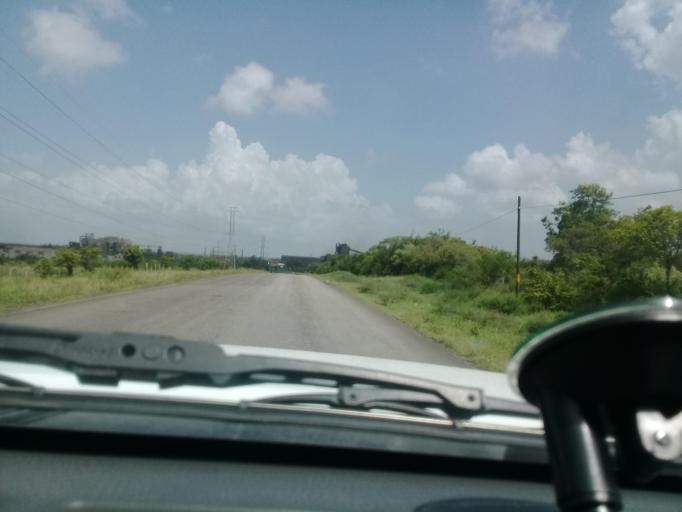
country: MX
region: Veracruz
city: Moralillo
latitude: 22.2281
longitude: -98.0148
